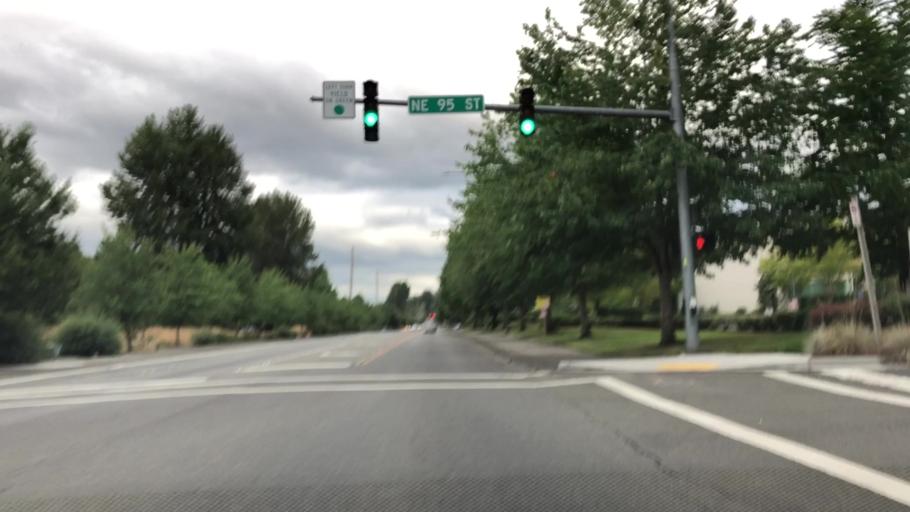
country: US
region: Washington
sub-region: King County
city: Redmond
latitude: 47.6855
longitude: -122.1457
